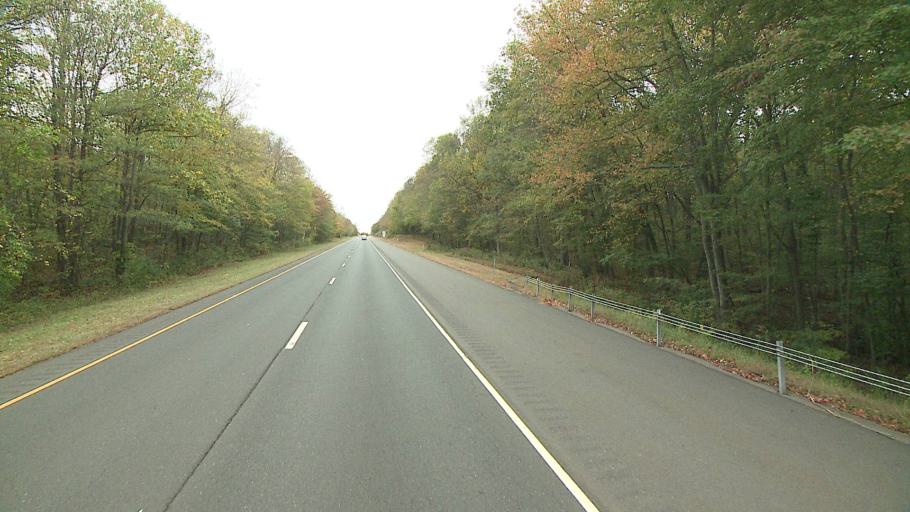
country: US
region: Connecticut
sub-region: Middlesex County
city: East Haddam
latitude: 41.4289
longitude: -72.5076
